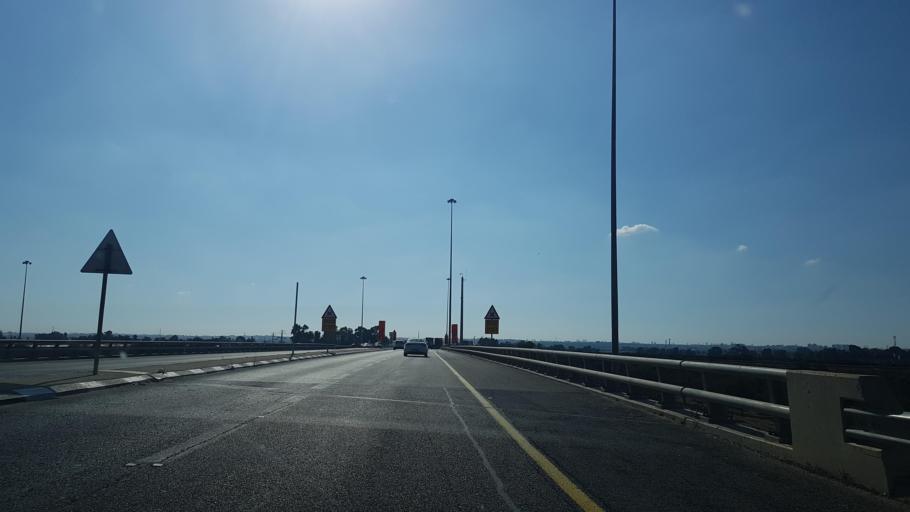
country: PS
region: West Bank
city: Tulkarm
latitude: 32.3140
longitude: 35.0138
